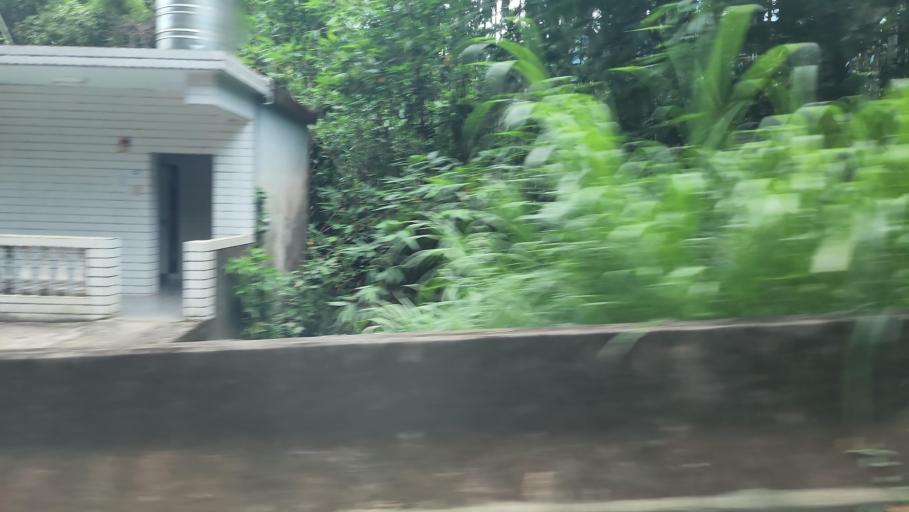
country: TW
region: Taipei
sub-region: Taipei
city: Banqiao
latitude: 24.9183
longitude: 121.4178
